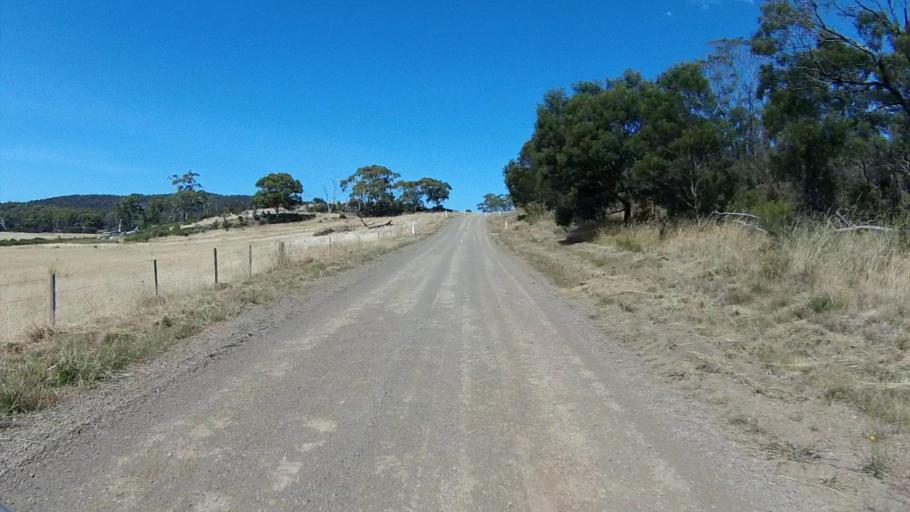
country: AU
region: Tasmania
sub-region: Break O'Day
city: St Helens
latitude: -41.9656
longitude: 148.0739
